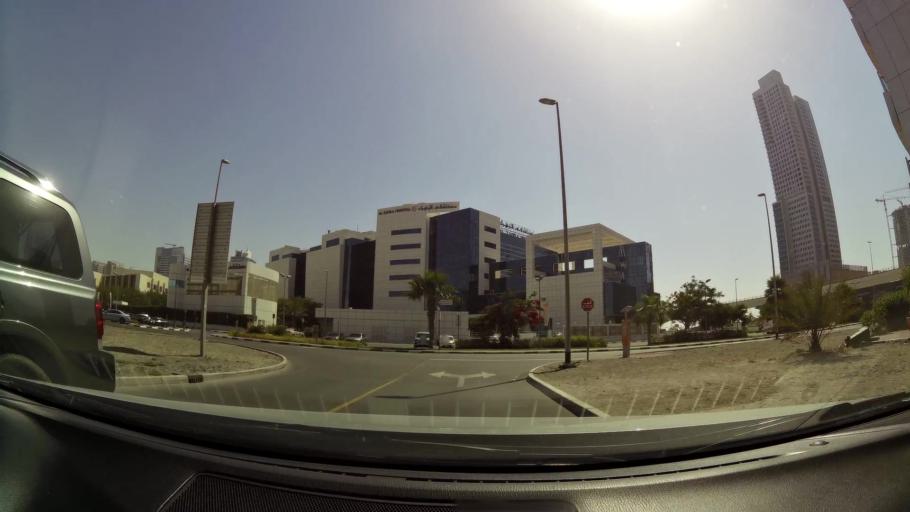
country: AE
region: Dubai
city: Dubai
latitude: 25.1069
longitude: 55.1819
